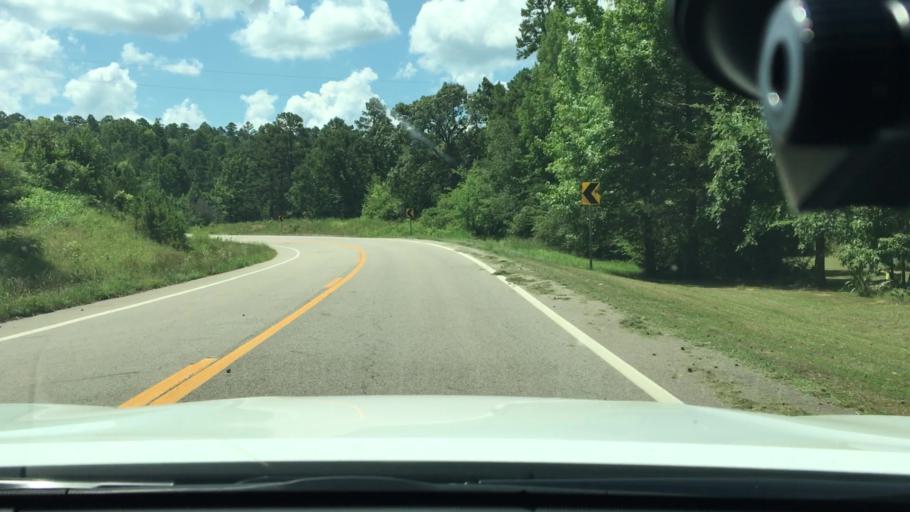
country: US
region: Arkansas
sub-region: Logan County
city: Paris
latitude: 35.2584
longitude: -93.6833
